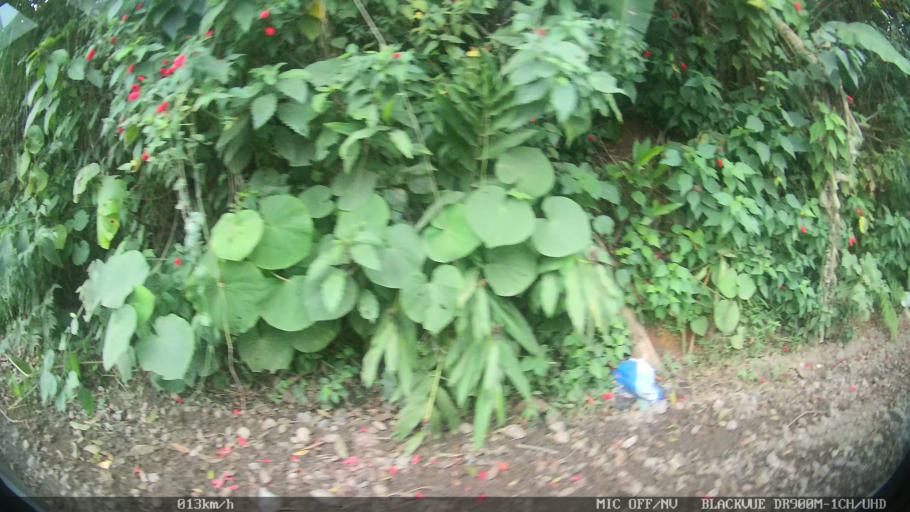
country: BR
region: Santa Catarina
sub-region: Joinville
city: Joinville
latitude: -26.3515
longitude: -48.8275
